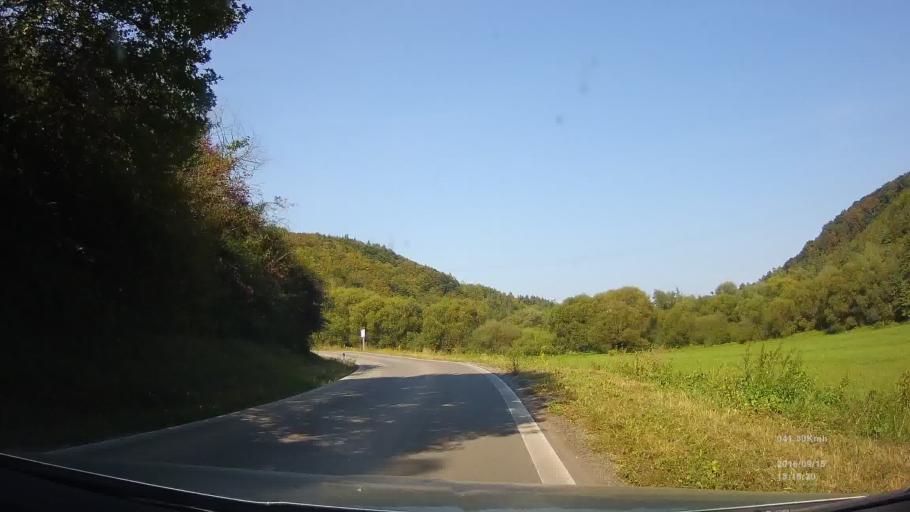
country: SK
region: Presovsky
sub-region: Okres Presov
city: Presov
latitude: 48.8960
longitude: 21.2043
